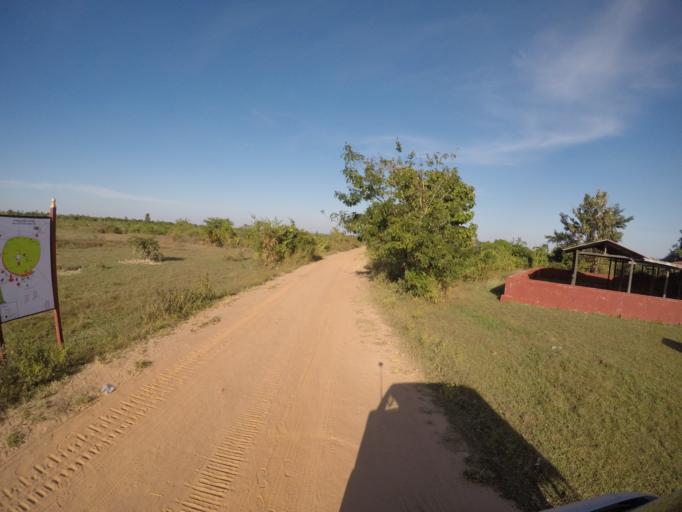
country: MM
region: Bago
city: Pyay
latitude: 18.7877
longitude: 95.2937
